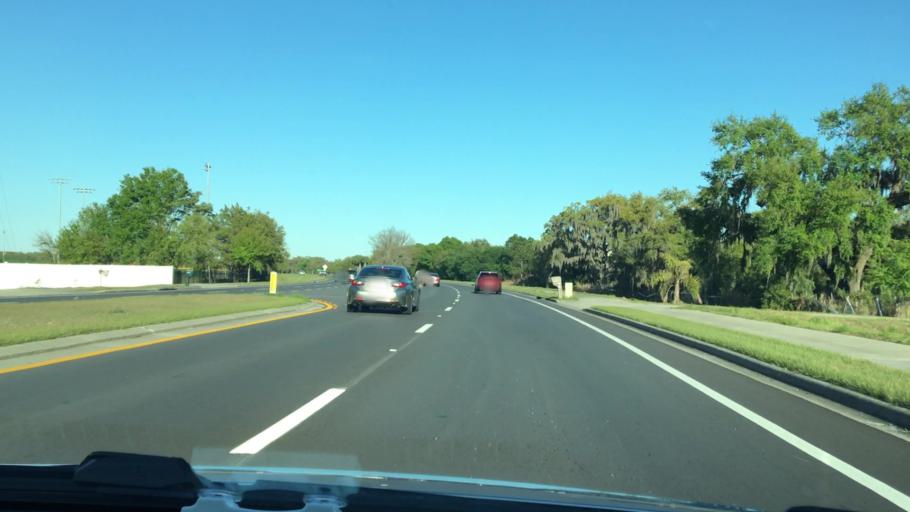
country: US
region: Florida
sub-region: Seminole County
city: Midway
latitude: 28.7604
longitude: -81.2200
